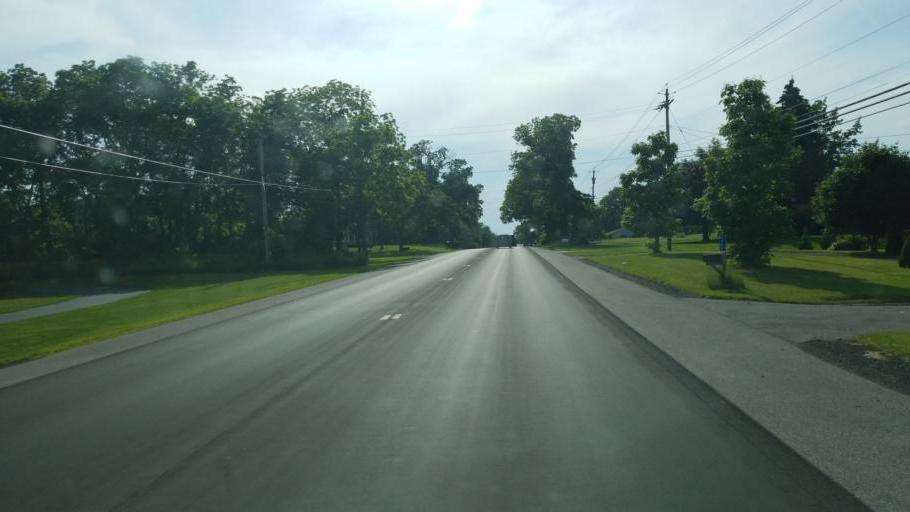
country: US
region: New York
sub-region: Genesee County
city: Batavia
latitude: 42.9848
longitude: -78.1007
